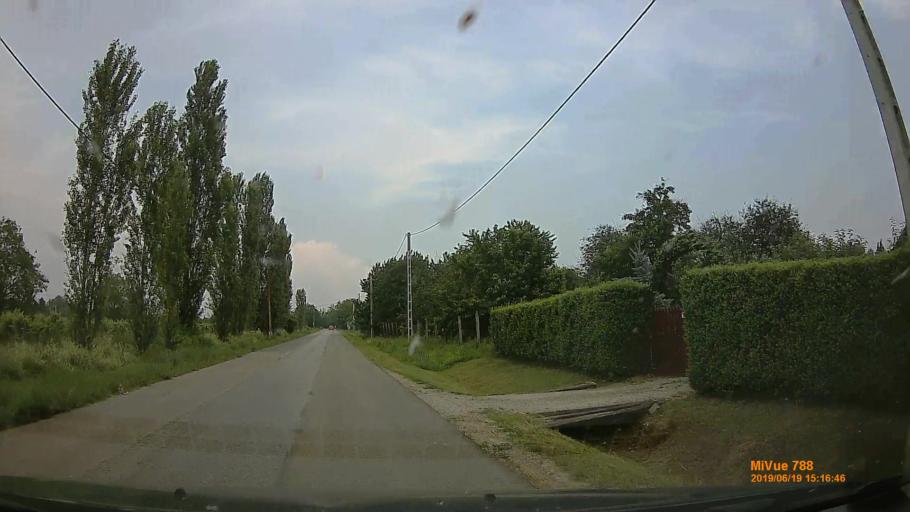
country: HU
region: Baranya
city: Szigetvar
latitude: 46.0790
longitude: 17.8431
